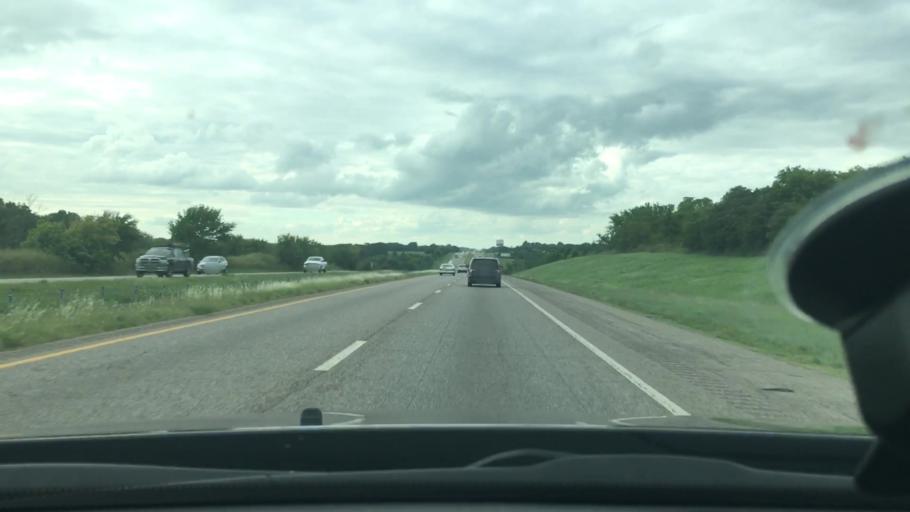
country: US
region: Oklahoma
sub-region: Cleveland County
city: Noble
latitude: 35.0987
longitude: -97.4262
